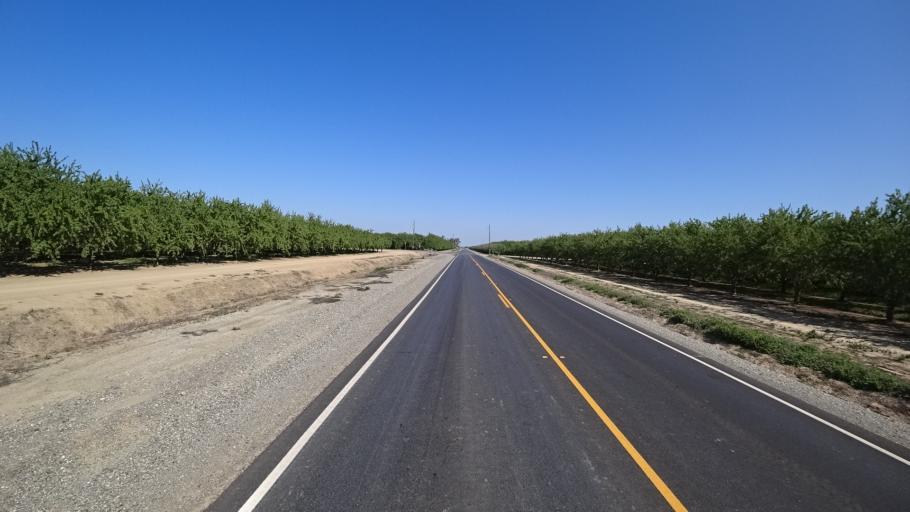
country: US
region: California
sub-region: Glenn County
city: Hamilton City
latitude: 39.6512
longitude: -122.0650
